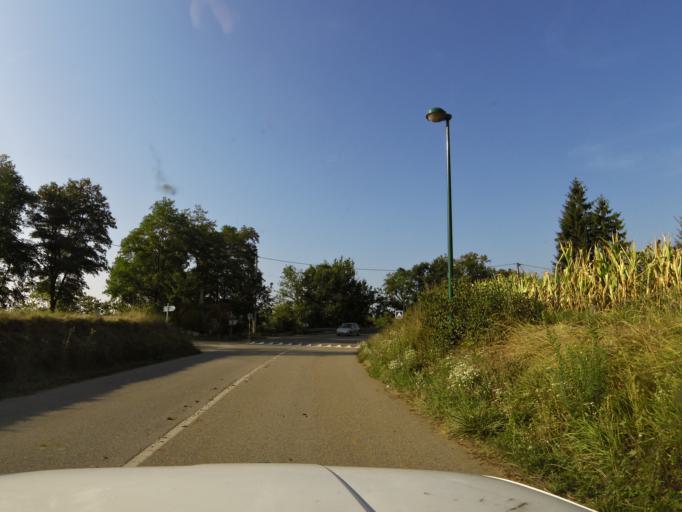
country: FR
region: Rhone-Alpes
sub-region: Departement de l'Ain
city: Chazey-sur-Ain
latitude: 45.8879
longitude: 5.2516
